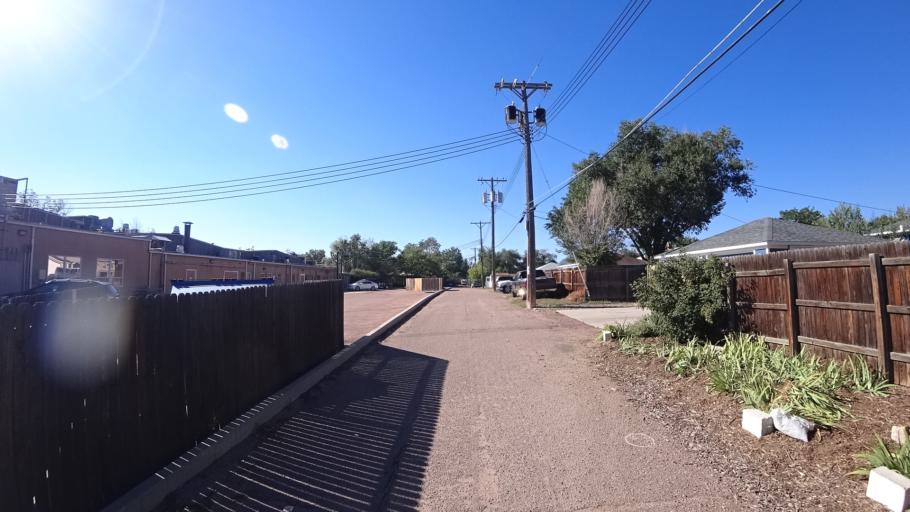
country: US
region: Colorado
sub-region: El Paso County
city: Colorado Springs
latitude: 38.8548
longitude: -104.8042
